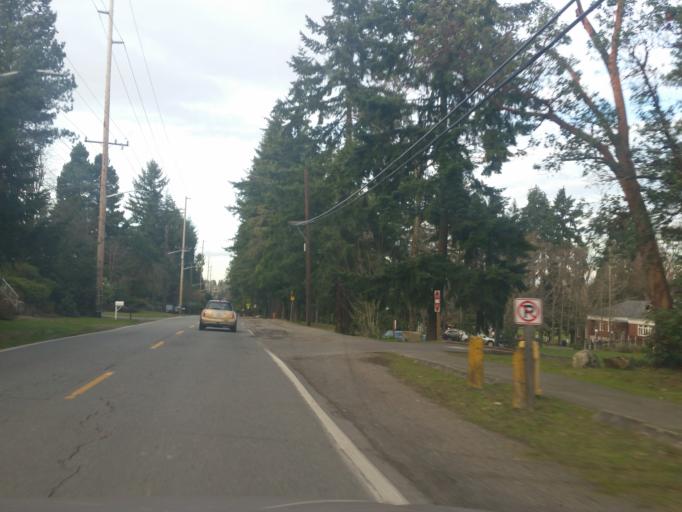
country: US
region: Washington
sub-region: King County
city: Shoreline
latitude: 47.7305
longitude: -122.3289
